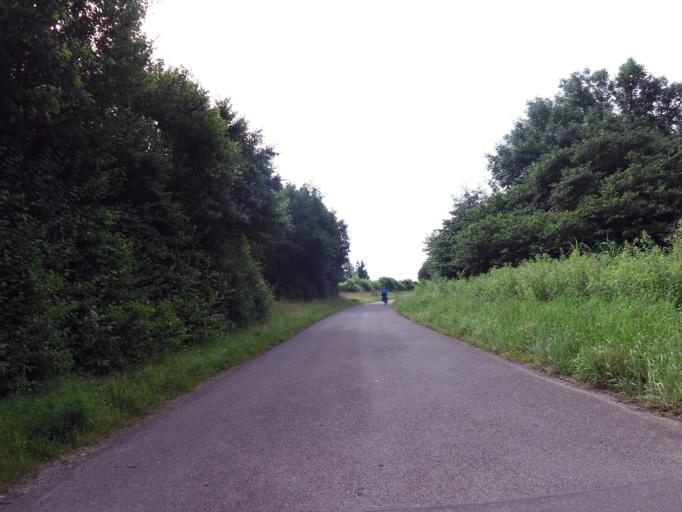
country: DE
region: Baden-Wuerttemberg
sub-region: Freiburg Region
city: Allensbach
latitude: 47.7274
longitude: 9.0388
